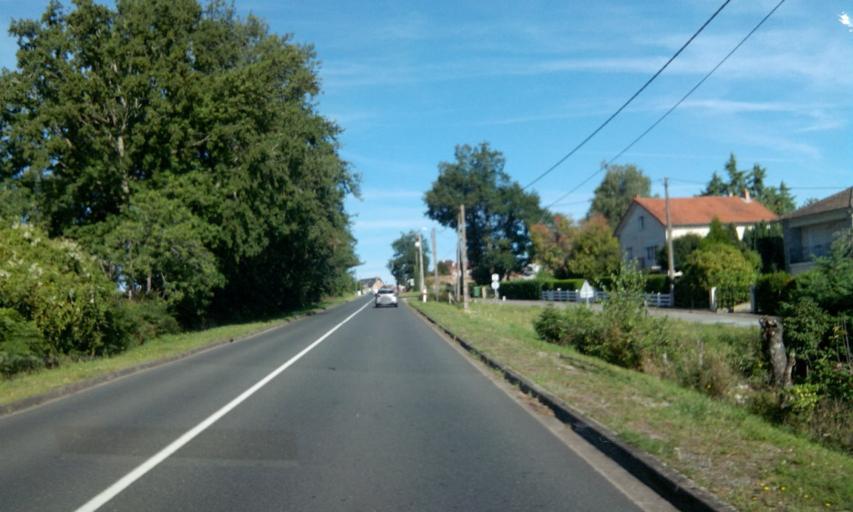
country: FR
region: Limousin
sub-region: Departement de la Haute-Vienne
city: Saint-Just-le-Martel
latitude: 45.8473
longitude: 1.4341
